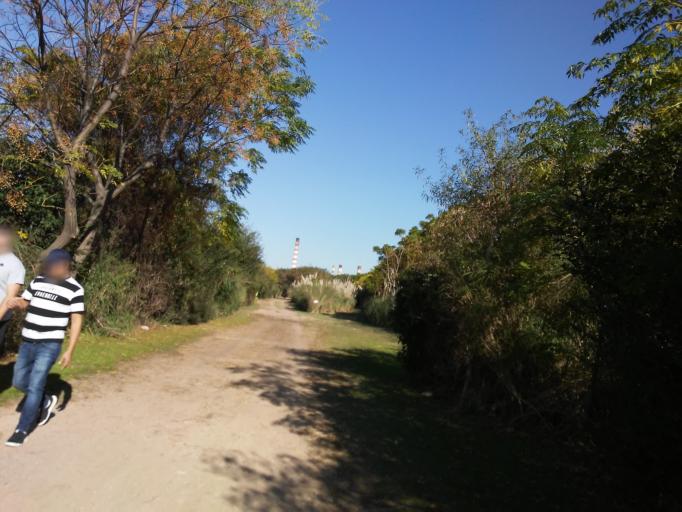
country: AR
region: Buenos Aires F.D.
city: Buenos Aires
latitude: -34.6129
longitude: -58.3406
